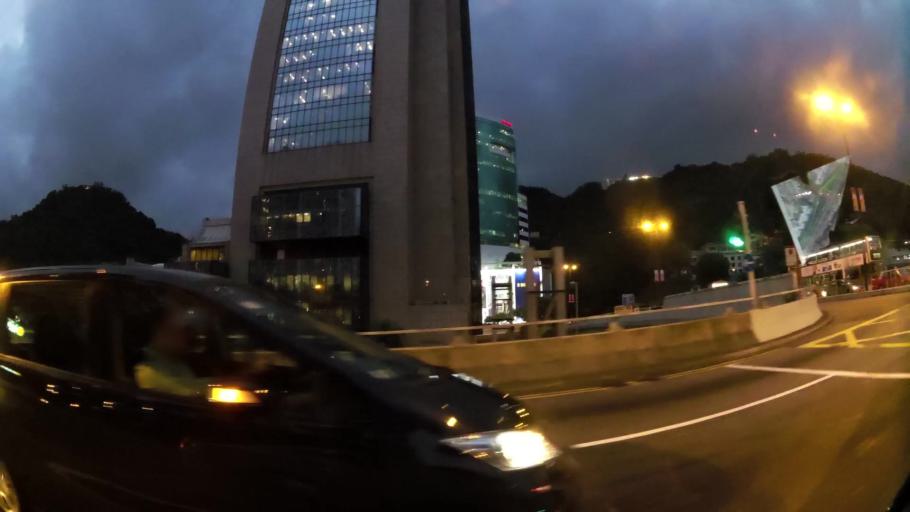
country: HK
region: Sha Tin
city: Sha Tin
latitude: 22.3848
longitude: 114.1893
